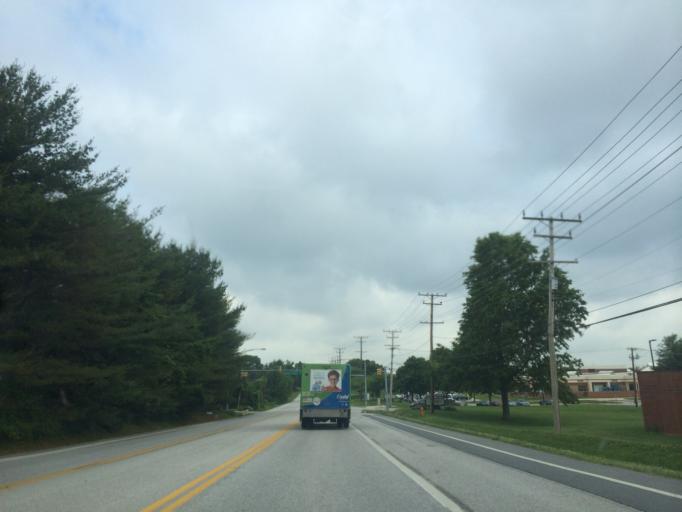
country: US
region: Maryland
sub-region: Howard County
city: Highland
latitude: 39.1890
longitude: -76.9244
